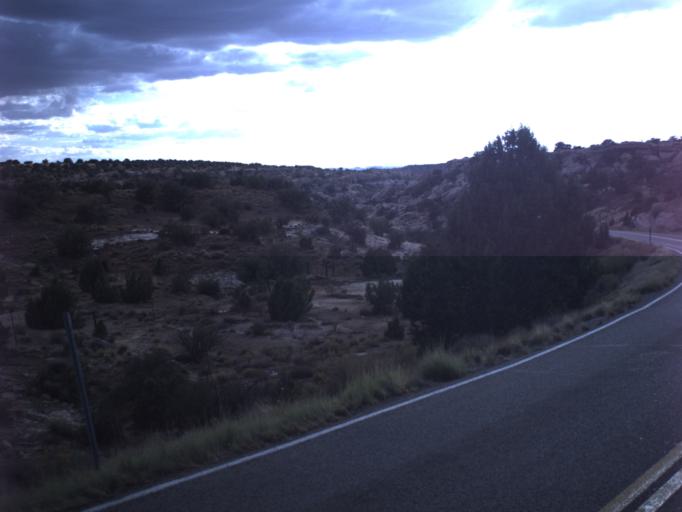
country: US
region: Utah
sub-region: San Juan County
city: Blanding
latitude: 37.4363
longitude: -109.3903
